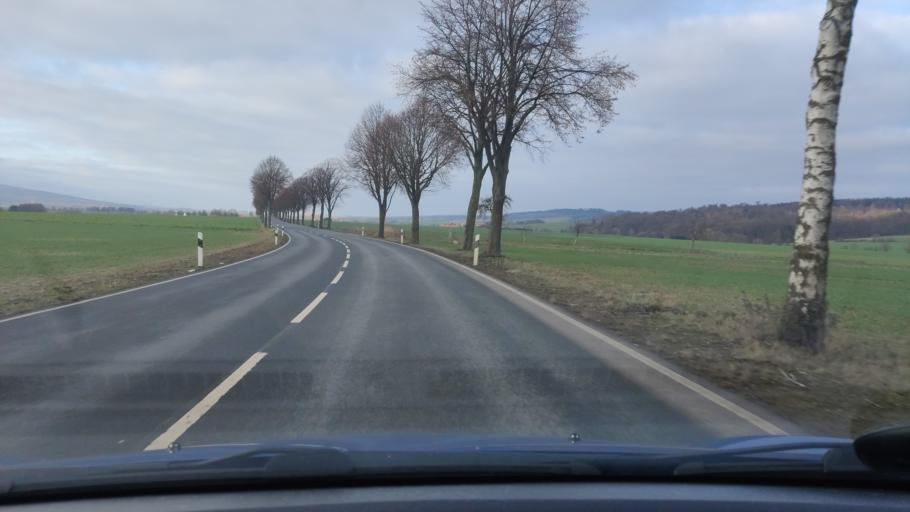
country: DE
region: Lower Saxony
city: Coppenbrugge
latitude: 52.1425
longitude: 9.5139
